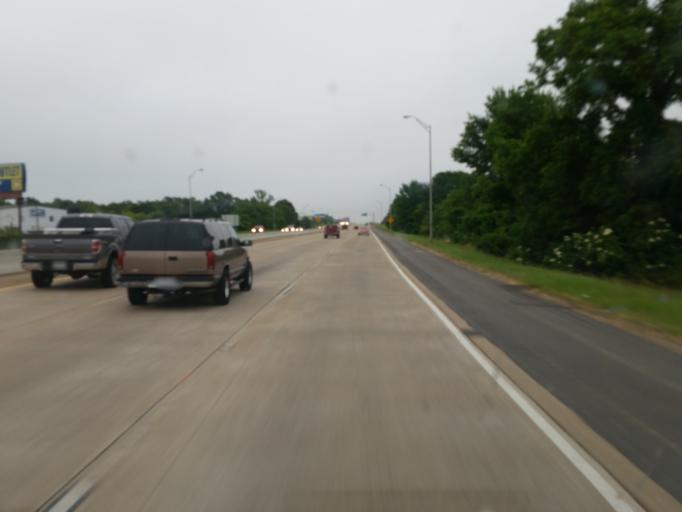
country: US
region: Louisiana
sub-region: Caddo Parish
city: Shreveport
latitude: 32.4674
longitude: -93.8122
